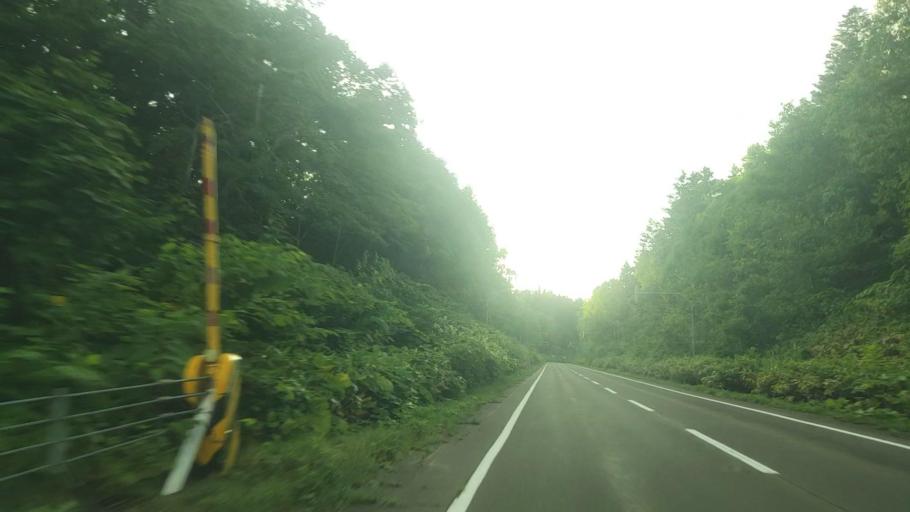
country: JP
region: Hokkaido
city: Bibai
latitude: 43.1404
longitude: 142.0946
